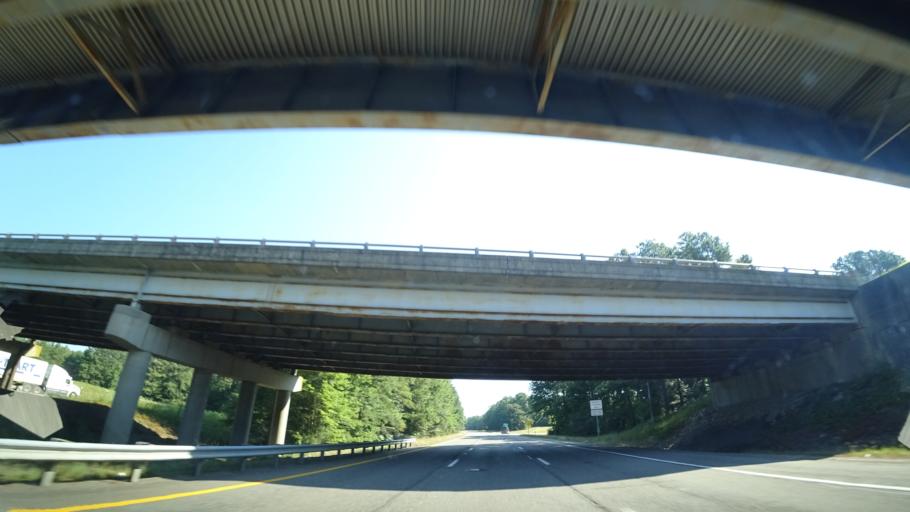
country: US
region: Virginia
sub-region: Henrico County
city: Sandston
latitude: 37.5094
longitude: -77.2737
